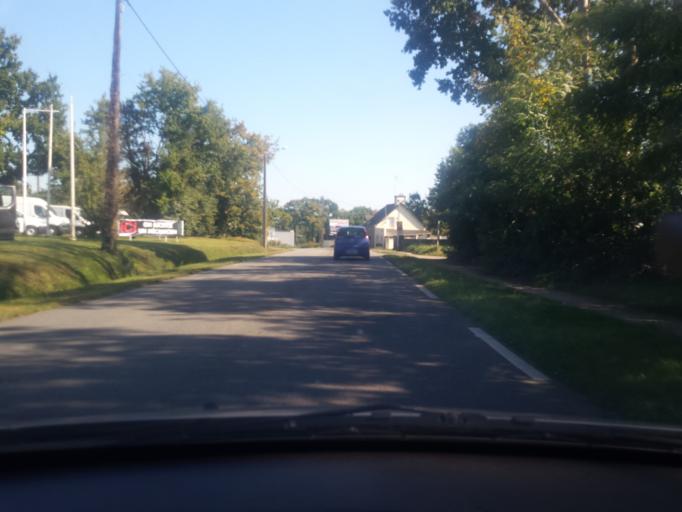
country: FR
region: Brittany
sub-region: Departement du Morbihan
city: Pontivy
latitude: 48.0596
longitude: -2.9541
